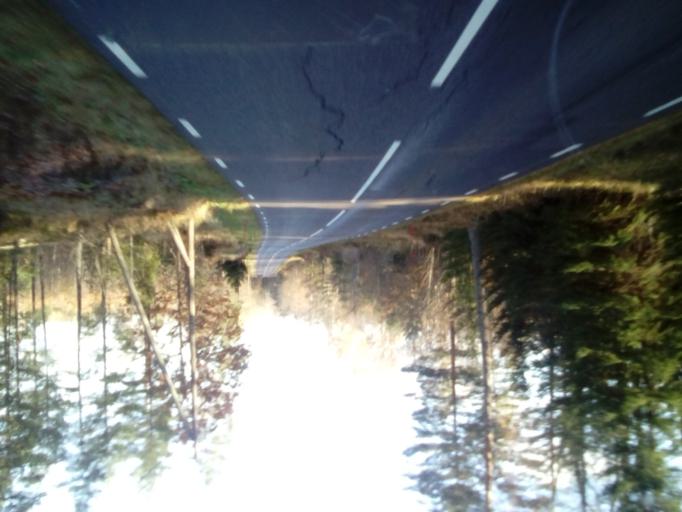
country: SE
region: Kalmar
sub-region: Vasterviks Kommun
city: Ankarsrum
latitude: 57.7374
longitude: 16.1024
